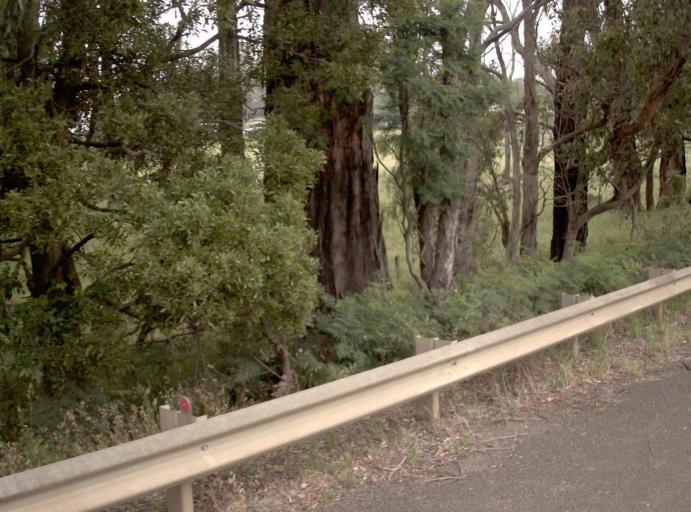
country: AU
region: Victoria
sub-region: Latrobe
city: Moe
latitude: -38.3344
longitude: 146.2238
